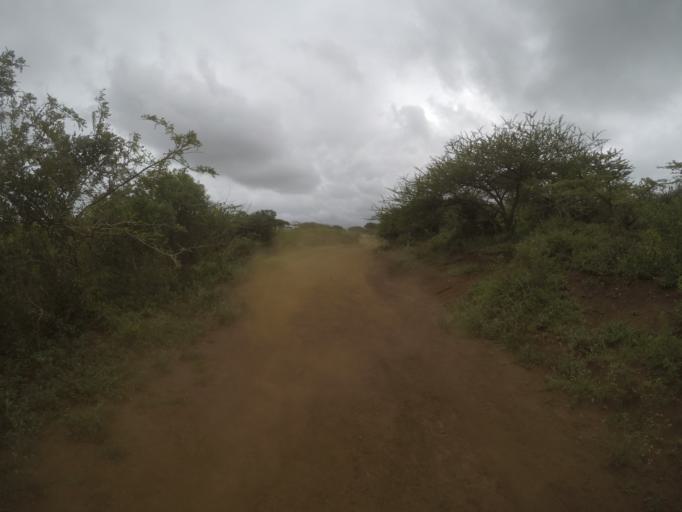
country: ZA
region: KwaZulu-Natal
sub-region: uThungulu District Municipality
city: Empangeni
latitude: -28.6007
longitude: 31.8515
